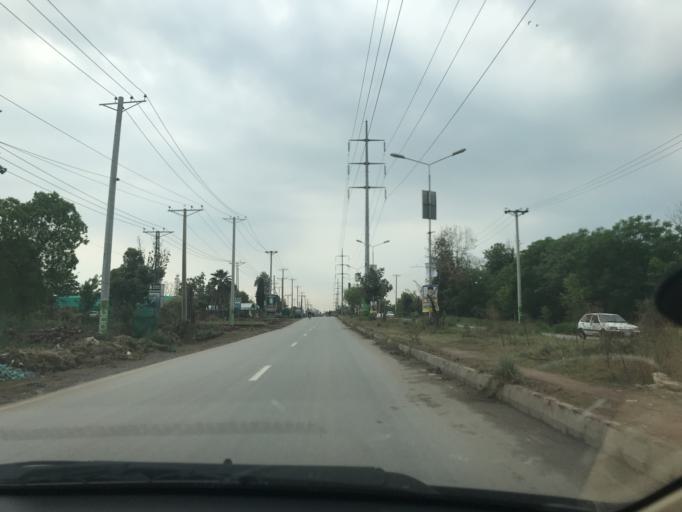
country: PK
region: Punjab
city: Rawalpindi
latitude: 33.6780
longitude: 73.1504
